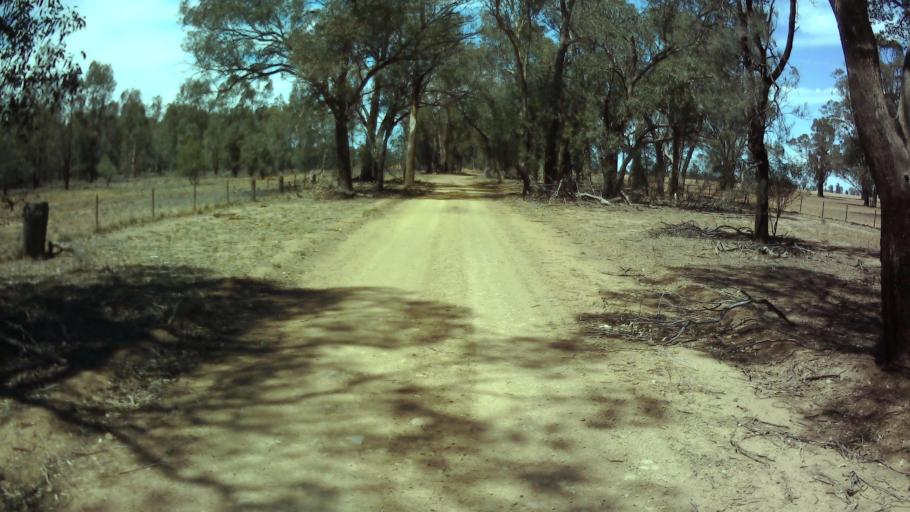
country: AU
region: New South Wales
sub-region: Weddin
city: Grenfell
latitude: -33.9122
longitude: 147.8064
